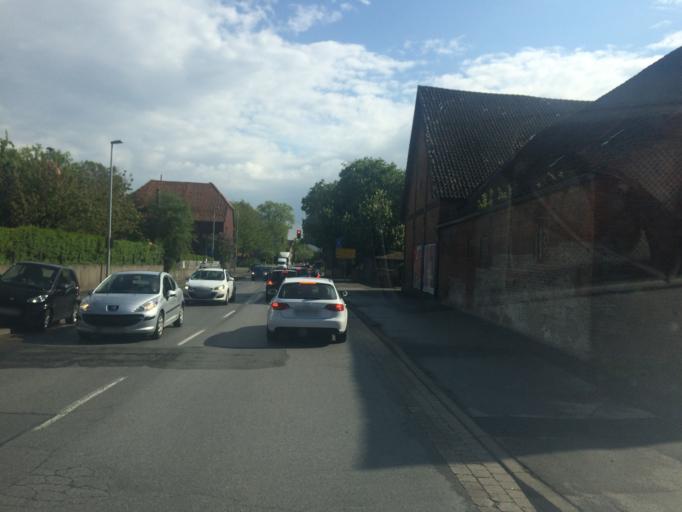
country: DE
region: Lower Saxony
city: Gross Munzel
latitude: 52.3664
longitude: 9.4789
